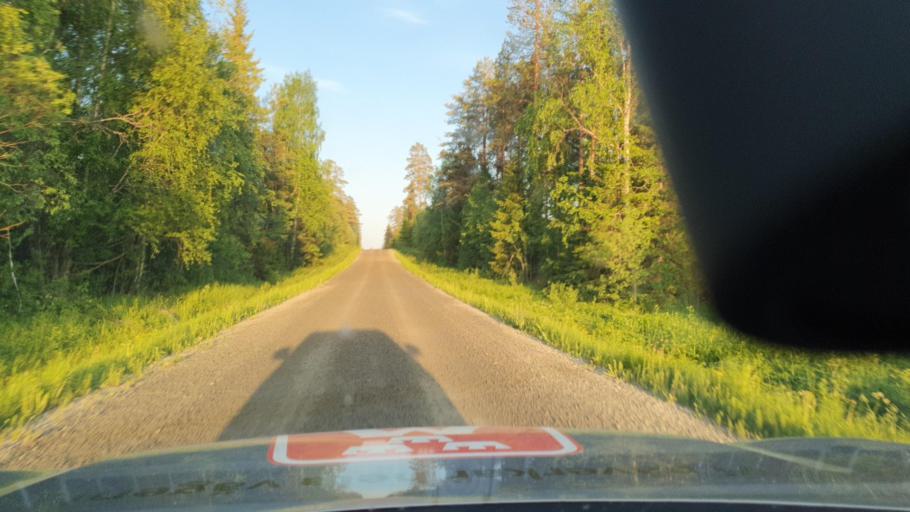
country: SE
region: Norrbotten
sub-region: Bodens Kommun
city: Boden
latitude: 66.0605
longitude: 21.7332
